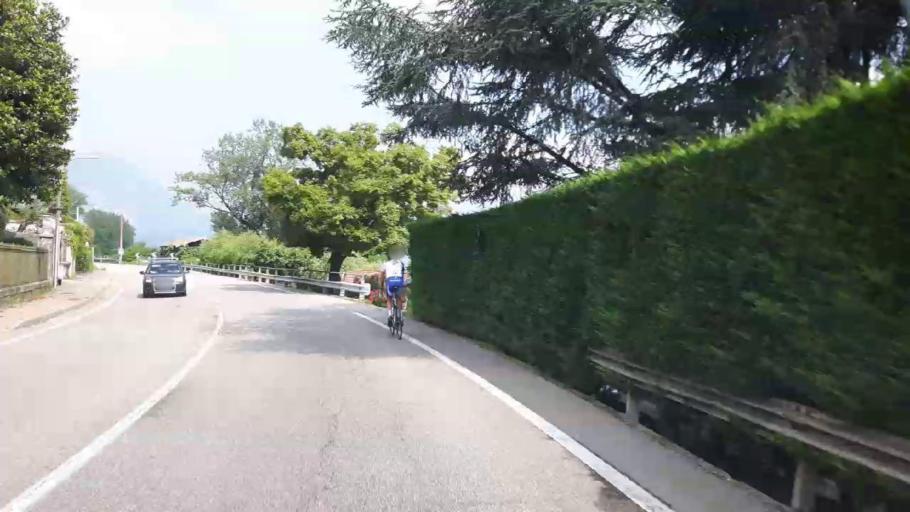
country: IT
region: Piedmont
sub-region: Provincia Verbano-Cusio-Ossola
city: Baveno
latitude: 45.9157
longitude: 8.5017
